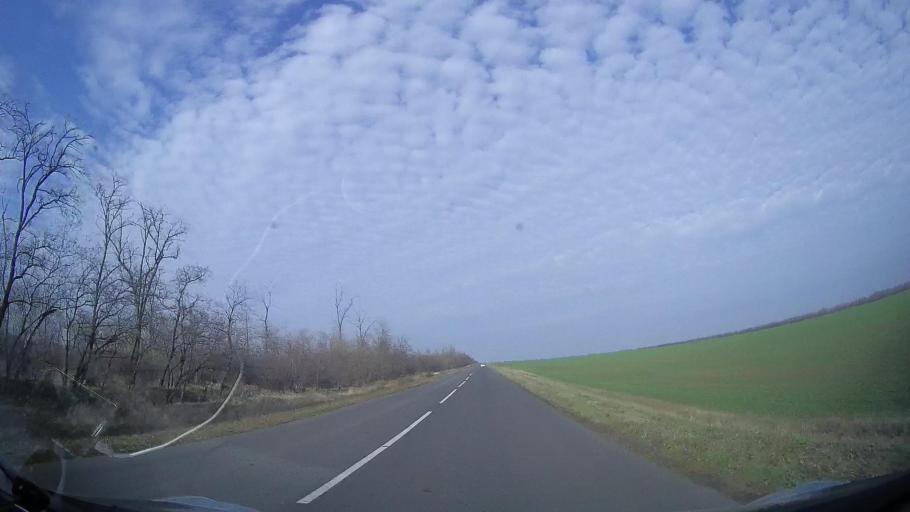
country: RU
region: Rostov
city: Gigant
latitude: 46.8474
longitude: 41.2864
